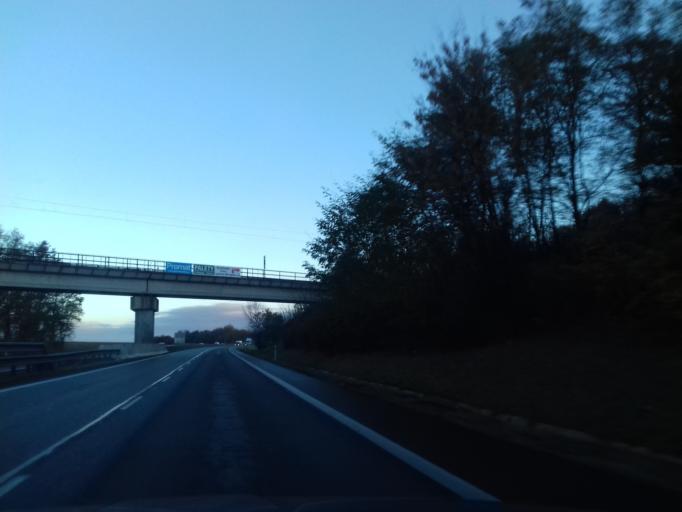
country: CZ
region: South Moravian
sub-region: Okres Vyskov
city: Vyskov
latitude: 49.2833
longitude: 17.0201
